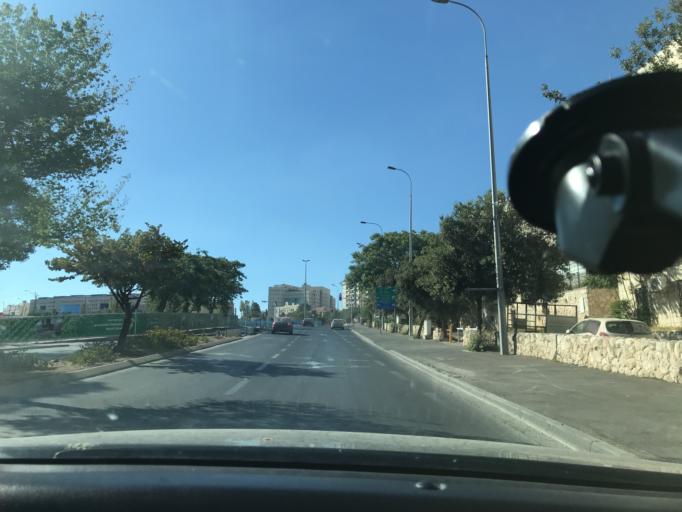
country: IL
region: Jerusalem
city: West Jerusalem
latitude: 31.7851
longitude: 35.2077
